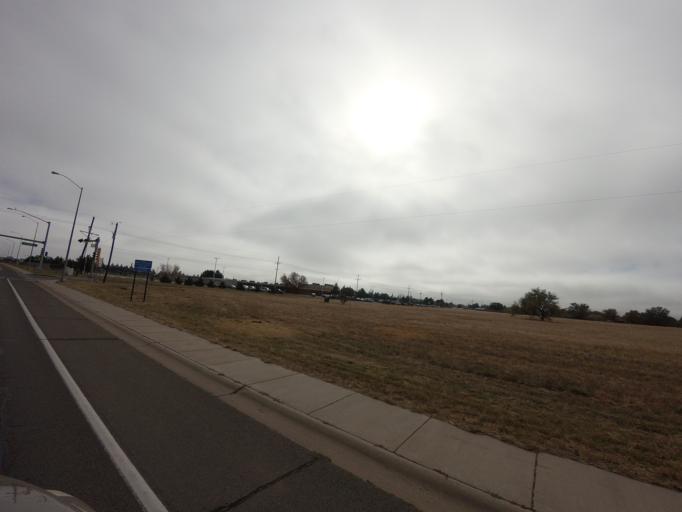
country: US
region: New Mexico
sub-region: Curry County
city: Clovis
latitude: 34.4339
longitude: -103.2147
